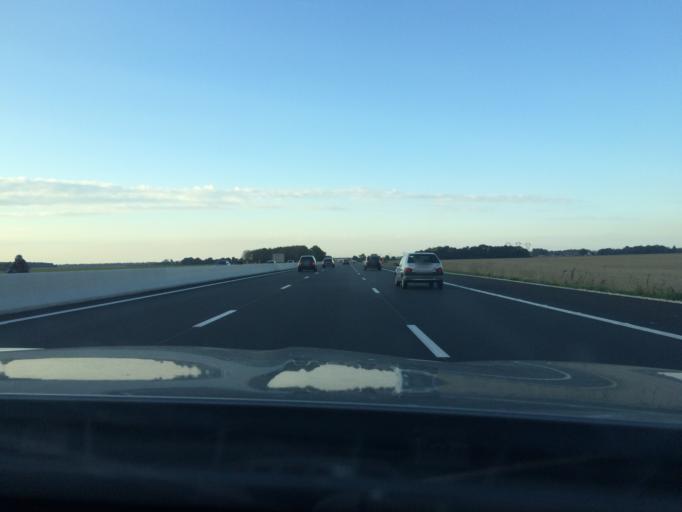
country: FR
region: Ile-de-France
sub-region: Departement de l'Essonne
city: Soisy-sur-Ecole
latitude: 48.5079
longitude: 2.5107
